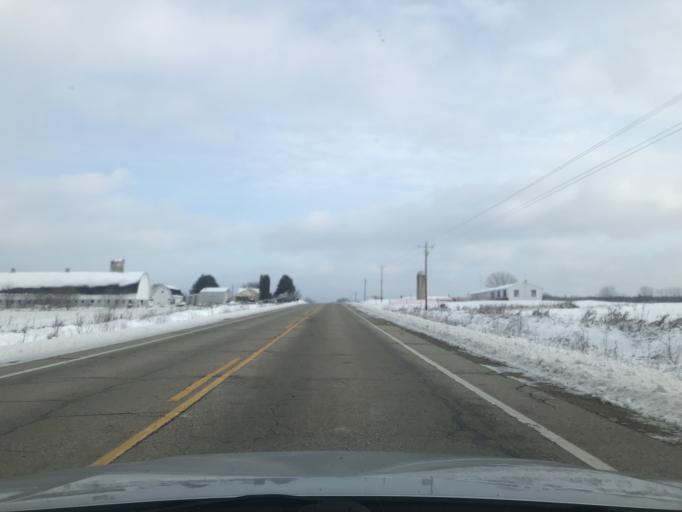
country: US
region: Wisconsin
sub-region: Oconto County
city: Oconto
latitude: 44.8933
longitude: -87.9882
